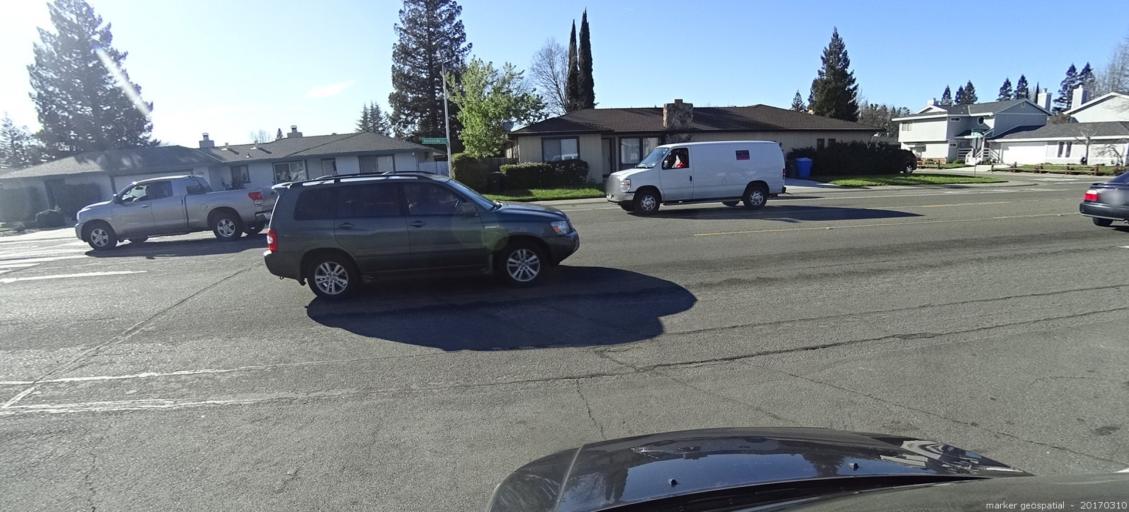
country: US
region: California
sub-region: Sacramento County
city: Parkway
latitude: 38.4959
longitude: -121.5313
